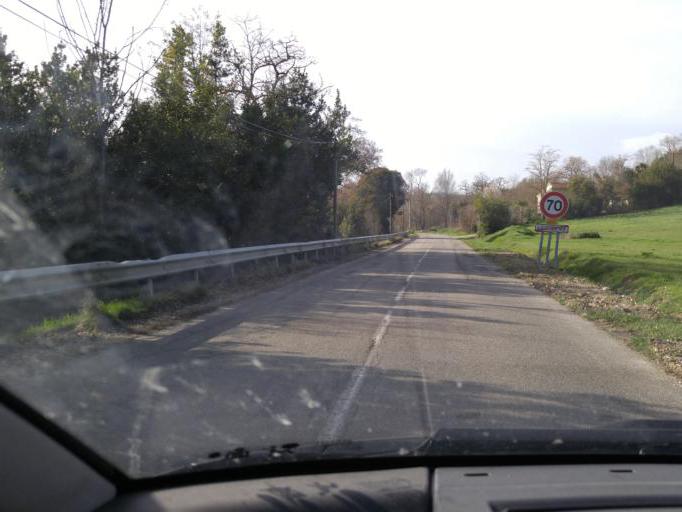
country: FR
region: Midi-Pyrenees
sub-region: Departement du Gers
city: Lectoure
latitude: 43.9305
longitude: 0.6228
